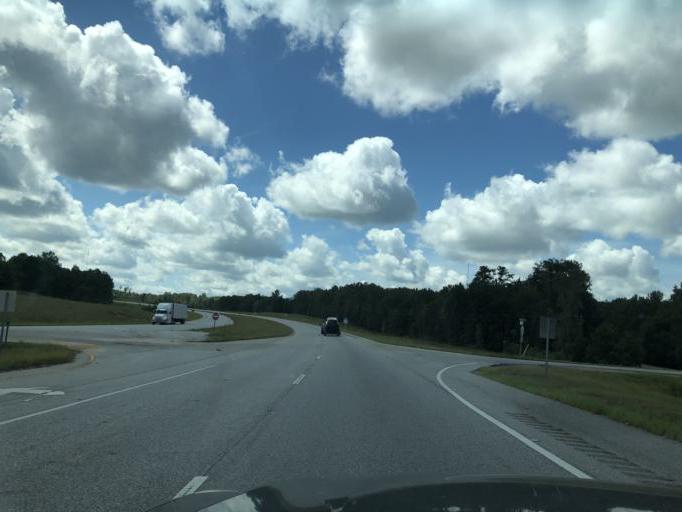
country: US
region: Alabama
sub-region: Barbour County
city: Eufaula
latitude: 32.1577
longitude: -85.1786
